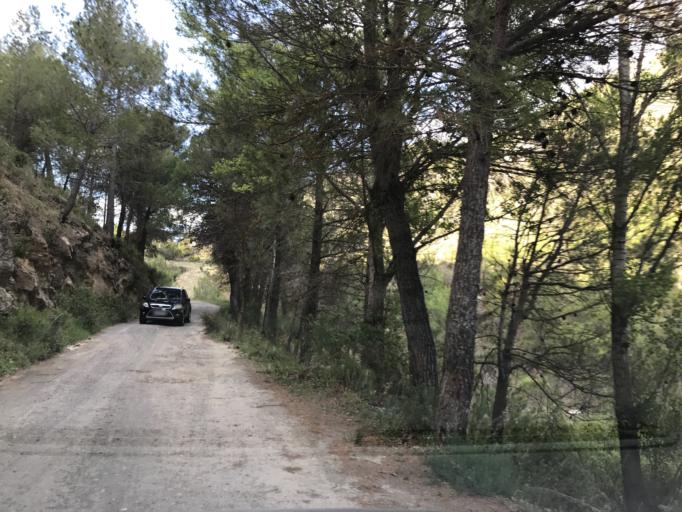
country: ES
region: Andalusia
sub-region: Provincia de Granada
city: Quentar
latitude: 37.2276
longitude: -3.4092
